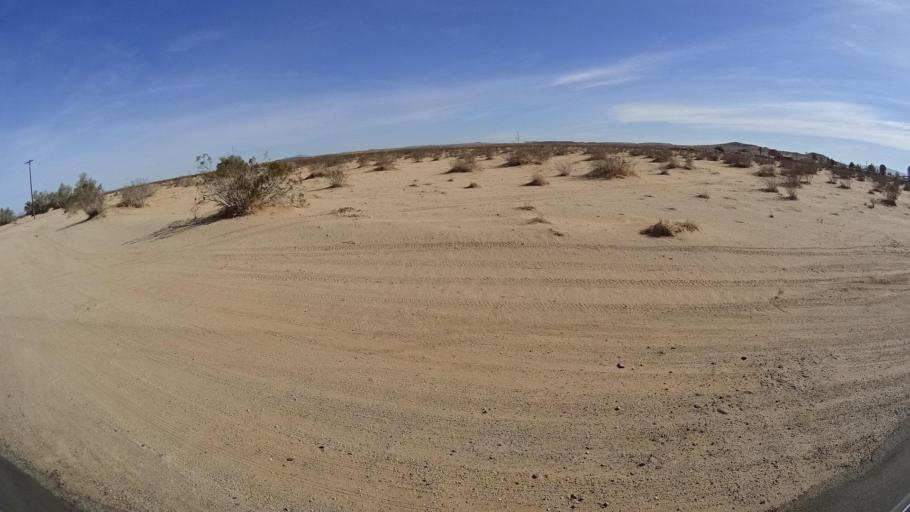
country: US
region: California
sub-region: Kern County
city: North Edwards
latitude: 35.0967
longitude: -117.7928
